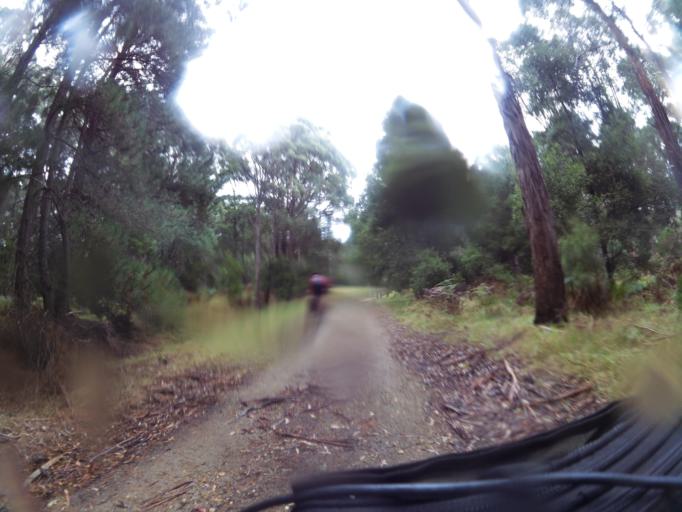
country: AU
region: New South Wales
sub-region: Greater Hume Shire
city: Holbrook
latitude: -36.1894
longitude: 147.5436
